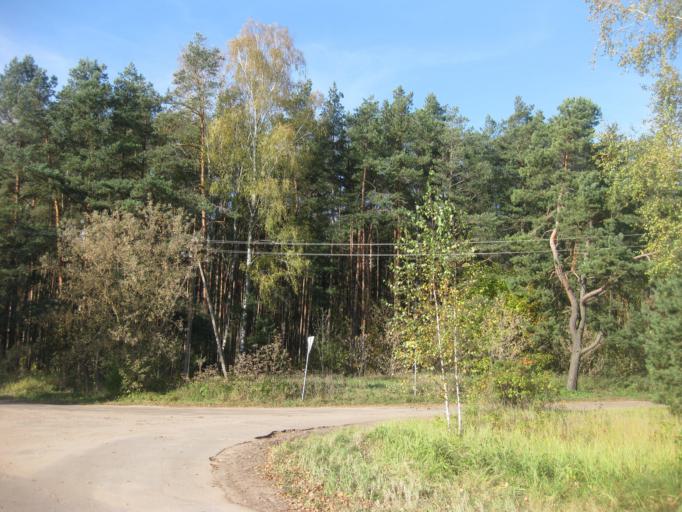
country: LT
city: Ezerelis
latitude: 54.8837
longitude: 23.5918
